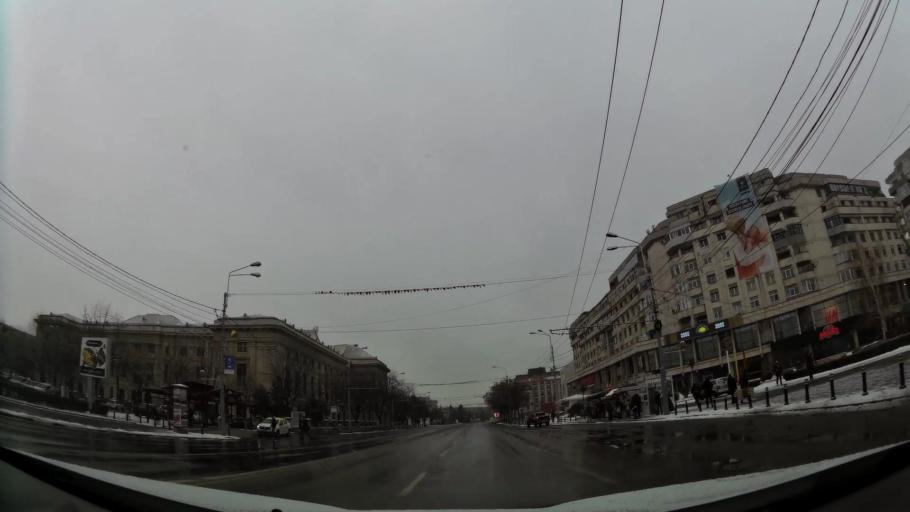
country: RO
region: Prahova
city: Ploiesti
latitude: 44.9421
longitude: 26.0205
